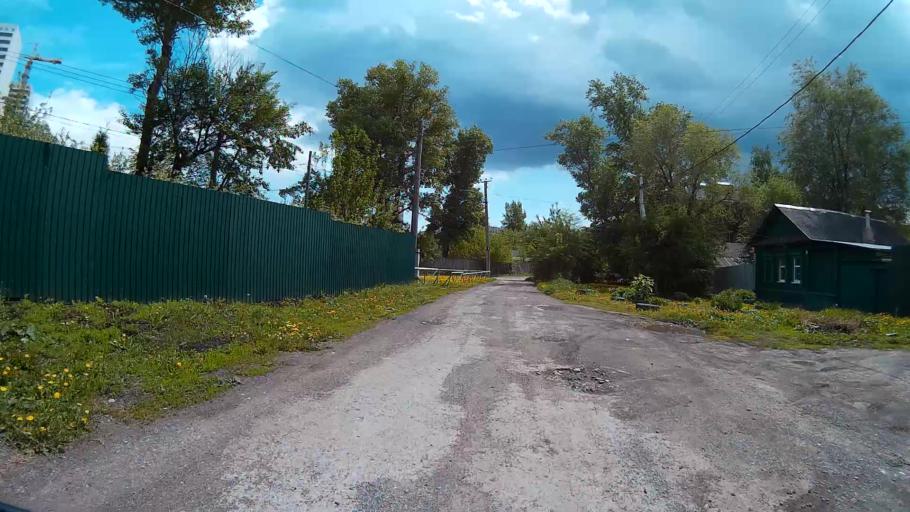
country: RU
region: Ulyanovsk
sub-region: Ulyanovskiy Rayon
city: Ulyanovsk
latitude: 54.3357
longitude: 48.3851
